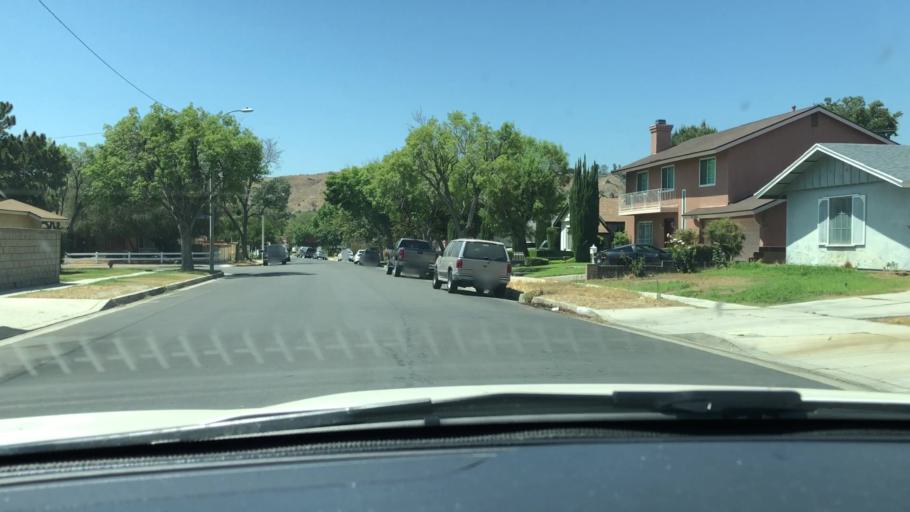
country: US
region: California
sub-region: Los Angeles County
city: Santa Clarita
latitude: 34.4236
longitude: -118.4846
